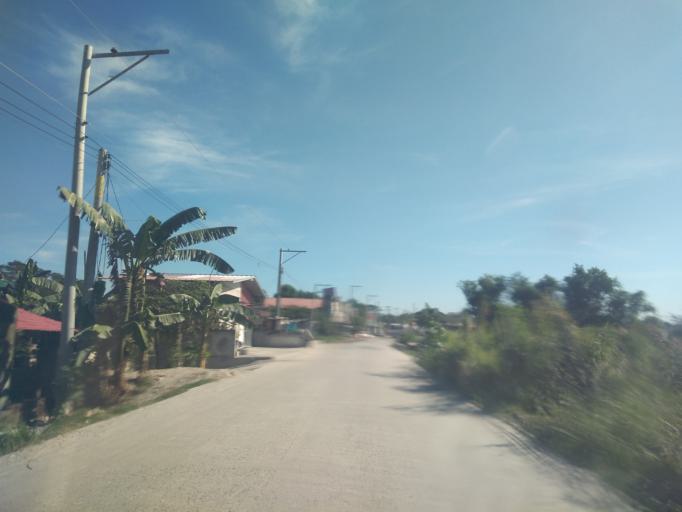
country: PH
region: Central Luzon
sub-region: Province of Pampanga
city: Bulaon
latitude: 15.0607
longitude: 120.6301
